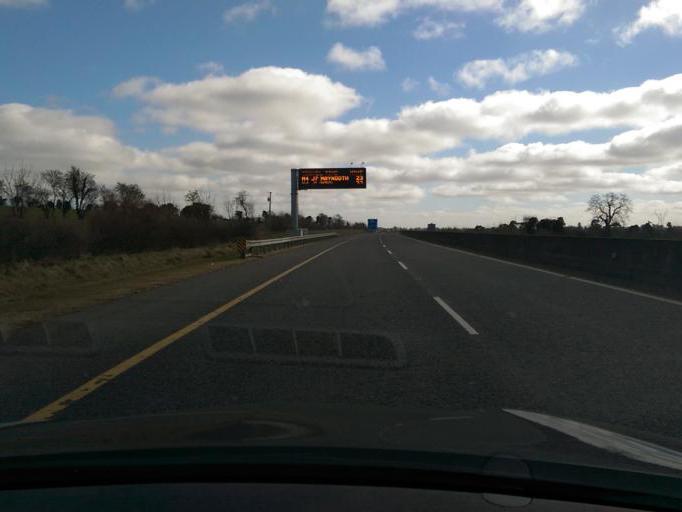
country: IE
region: Leinster
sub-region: An Iarmhi
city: Kinnegad
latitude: 53.4500
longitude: -7.1450
